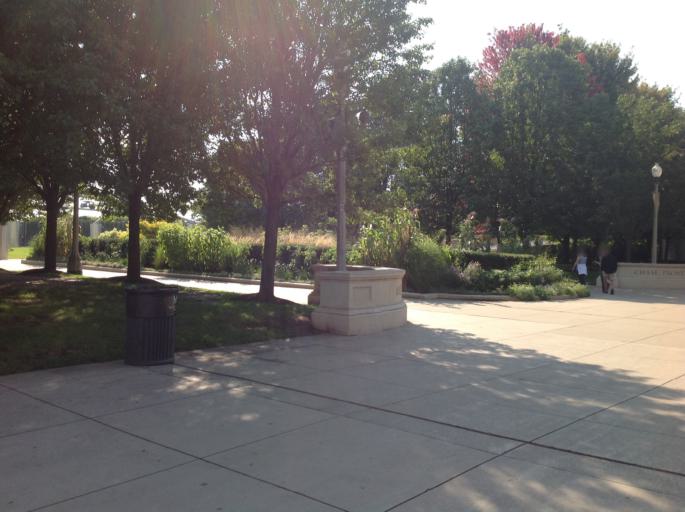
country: US
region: Illinois
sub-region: Cook County
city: Chicago
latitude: 41.8823
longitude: -87.6230
